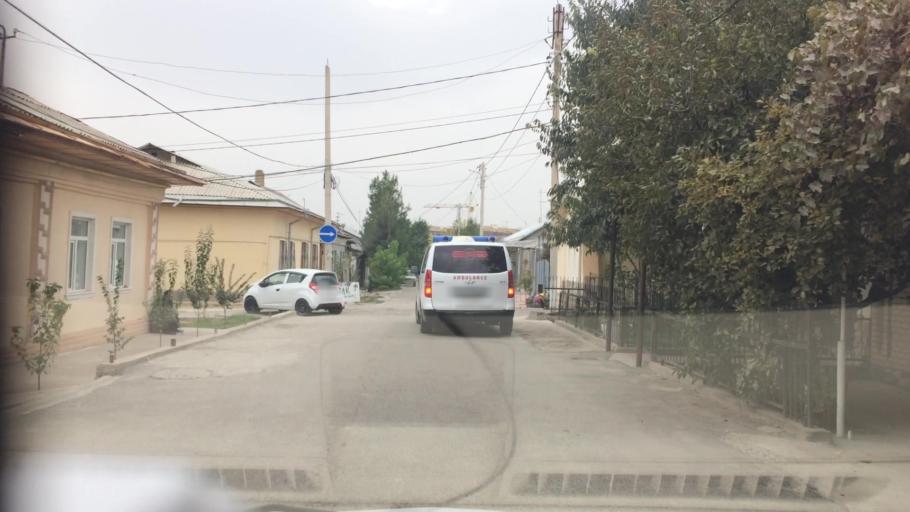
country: UZ
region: Toshkent
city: Salor
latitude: 41.3084
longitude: 69.3351
